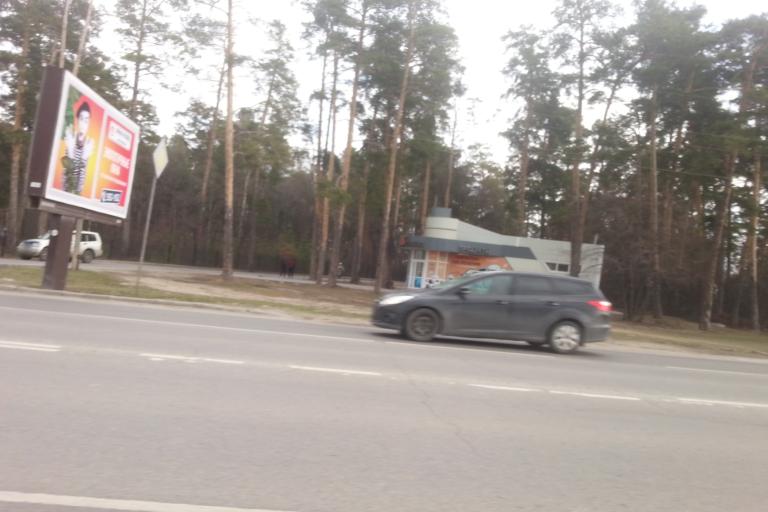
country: RU
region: Altai Krai
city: Zaton
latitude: 53.2804
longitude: 83.7486
